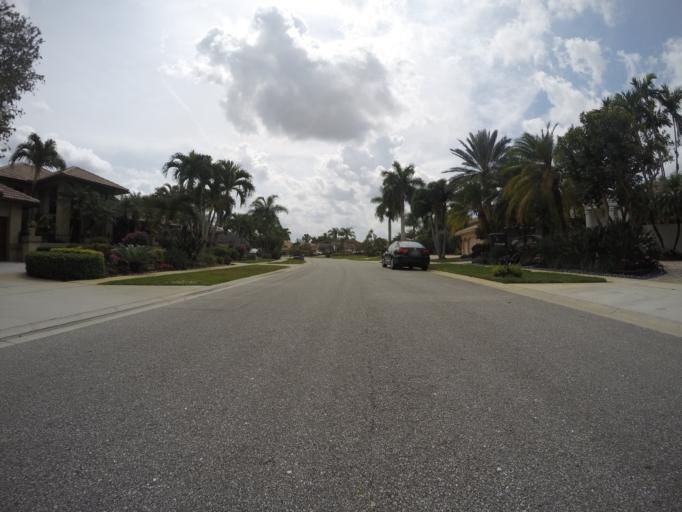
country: US
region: Florida
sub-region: Palm Beach County
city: Villages of Oriole
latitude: 26.4123
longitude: -80.2229
